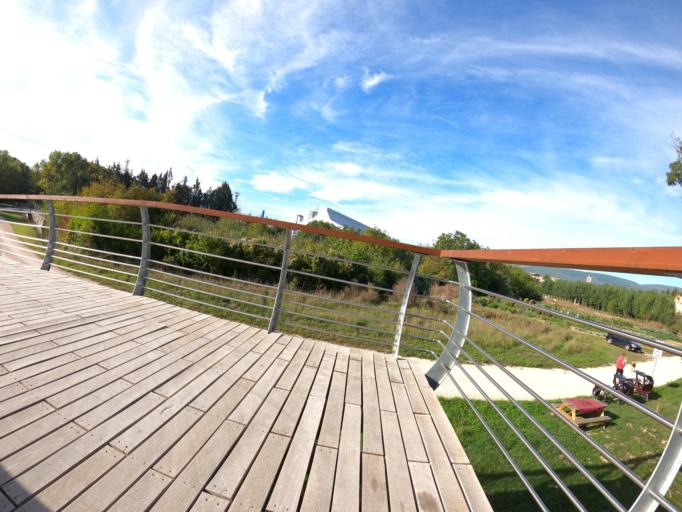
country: ES
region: Navarre
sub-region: Provincia de Navarra
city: Orkoien
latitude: 42.8170
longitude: -1.7407
